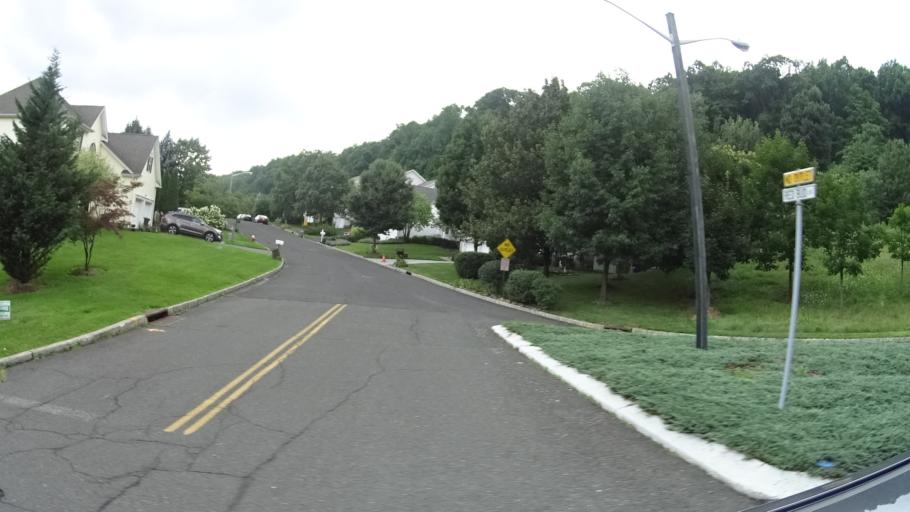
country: US
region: New Jersey
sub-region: Middlesex County
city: Dunellen
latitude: 40.5994
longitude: -74.4903
